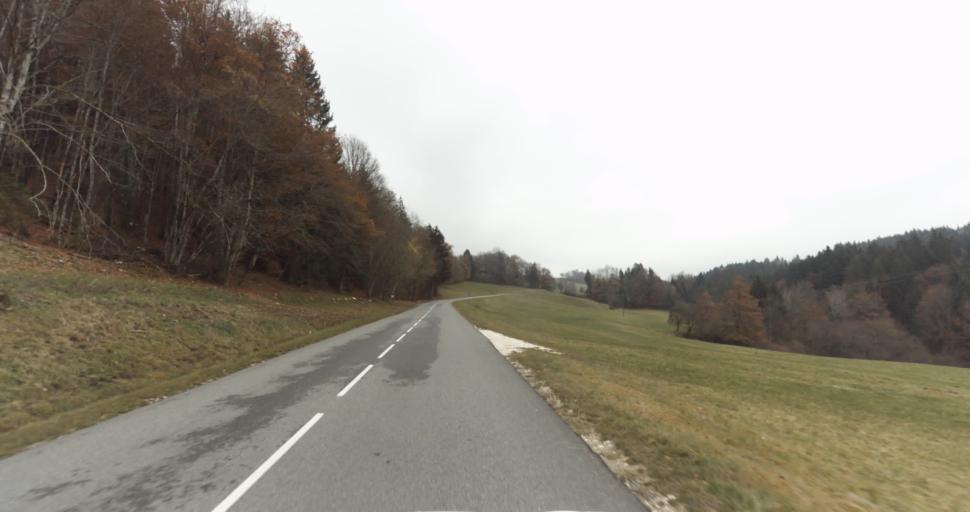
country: FR
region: Rhone-Alpes
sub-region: Departement de la Haute-Savoie
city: Gruffy
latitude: 45.7571
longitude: 6.1176
